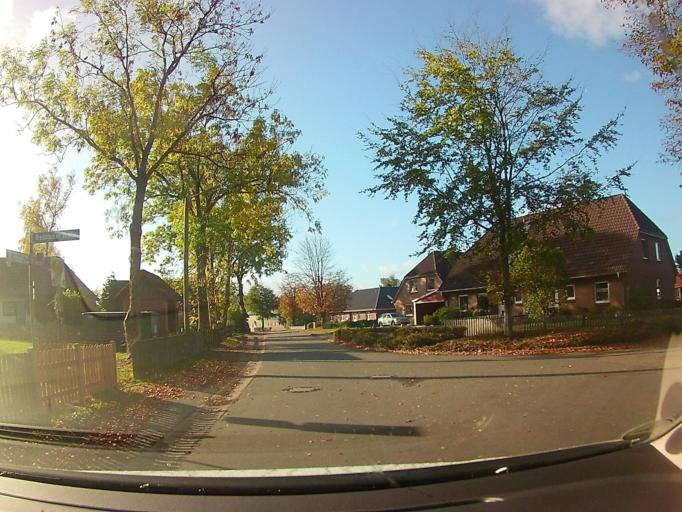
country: DE
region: Schleswig-Holstein
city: Breklum
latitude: 54.6146
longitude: 8.9874
